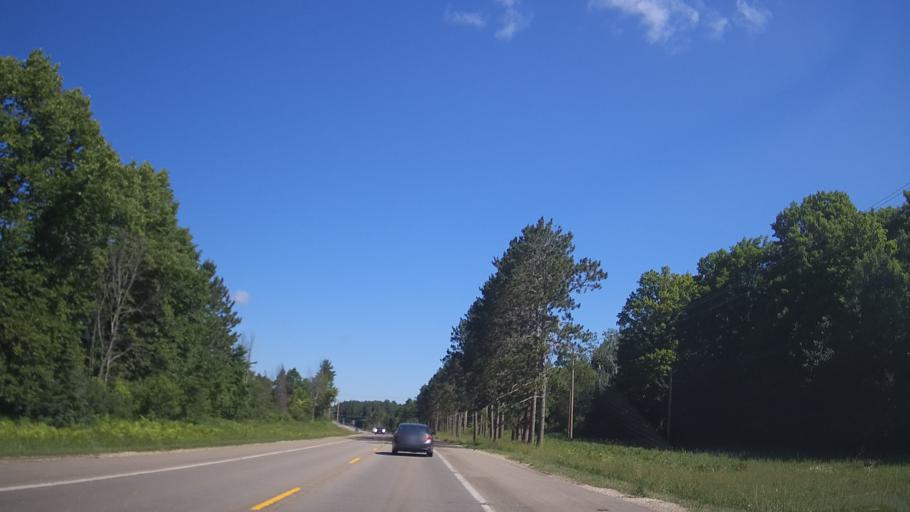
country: US
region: Michigan
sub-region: Cheboygan County
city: Indian River
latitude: 45.5339
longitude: -84.7820
